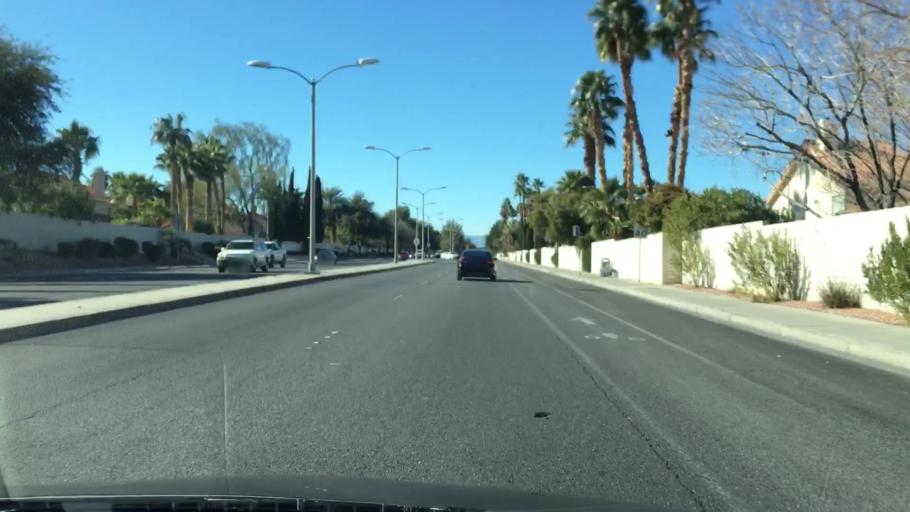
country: US
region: Nevada
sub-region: Clark County
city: Whitney
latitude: 36.0563
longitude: -115.0691
